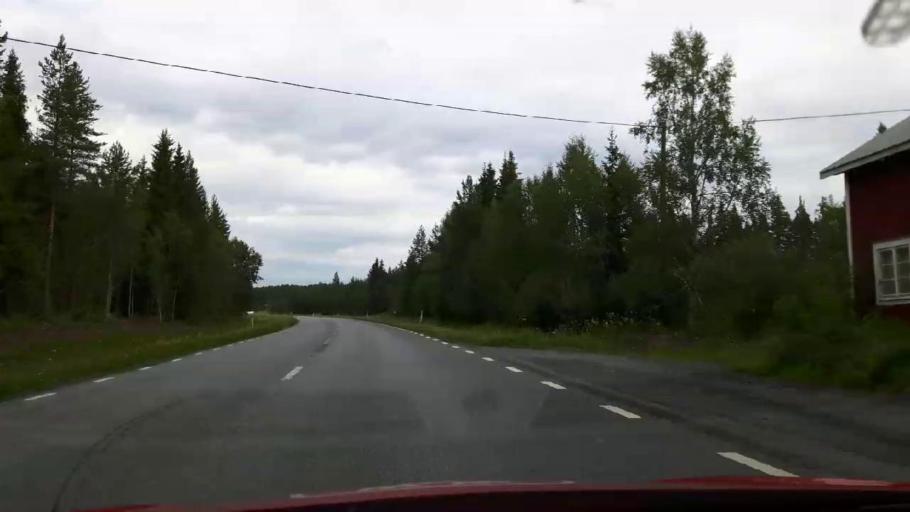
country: SE
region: Jaemtland
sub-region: Stroemsunds Kommun
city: Stroemsund
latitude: 63.5542
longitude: 15.3734
